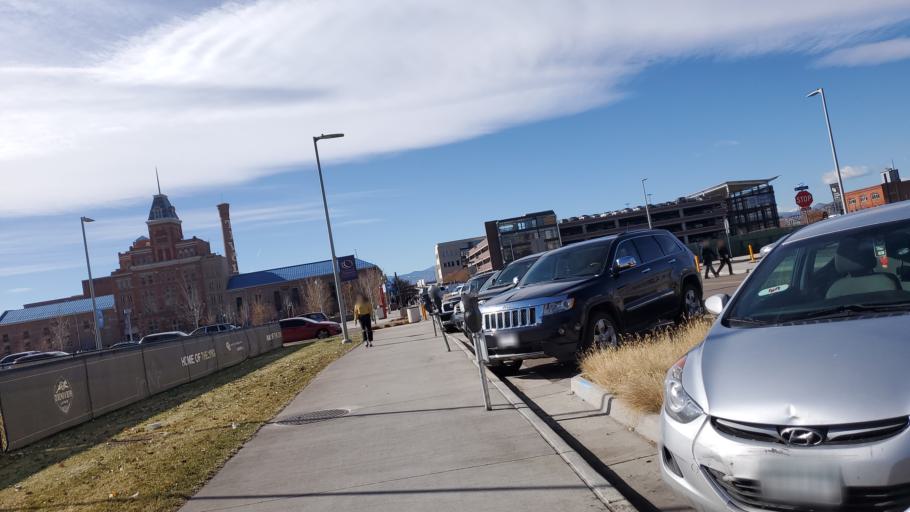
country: US
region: Colorado
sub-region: Denver County
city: Denver
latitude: 39.7467
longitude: -105.0041
